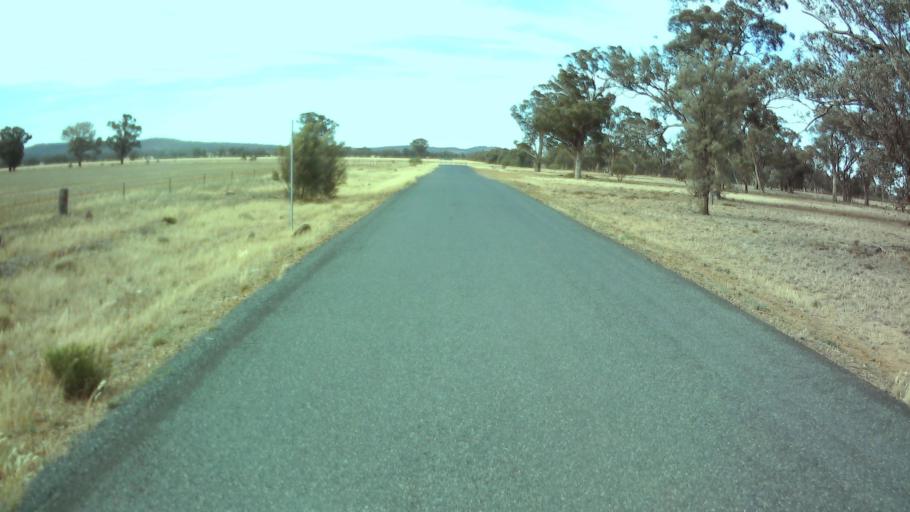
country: AU
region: New South Wales
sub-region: Weddin
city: Grenfell
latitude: -33.8583
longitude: 147.8604
